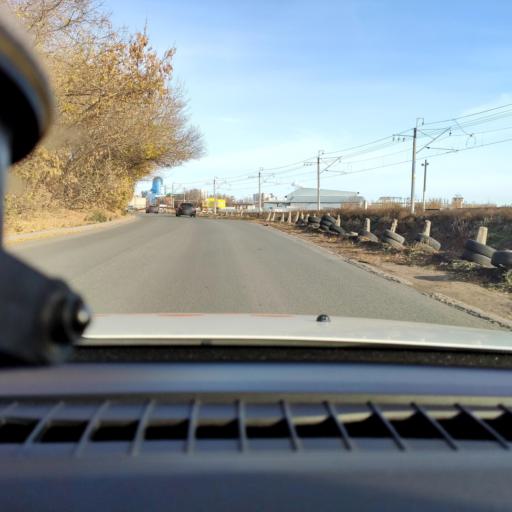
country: RU
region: Samara
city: Samara
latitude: 53.1809
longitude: 50.1067
